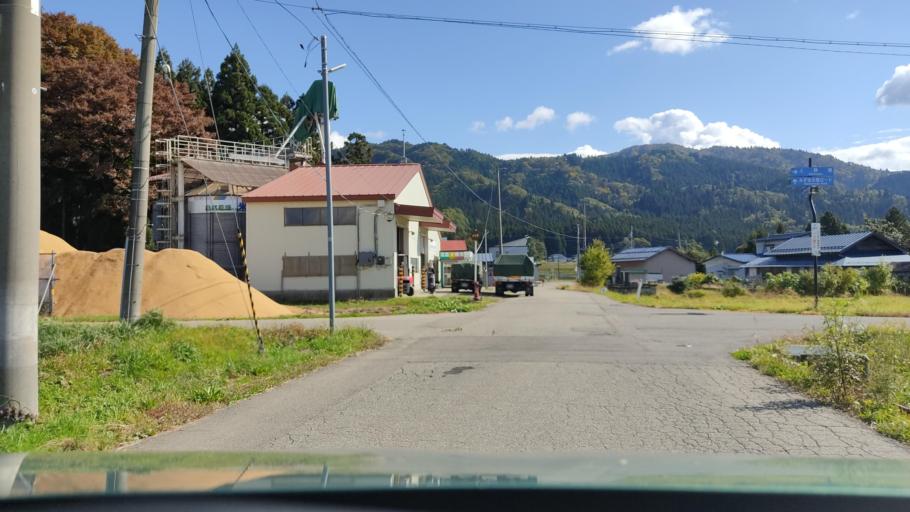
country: JP
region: Akita
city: Yokotemachi
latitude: 39.4032
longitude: 140.5832
